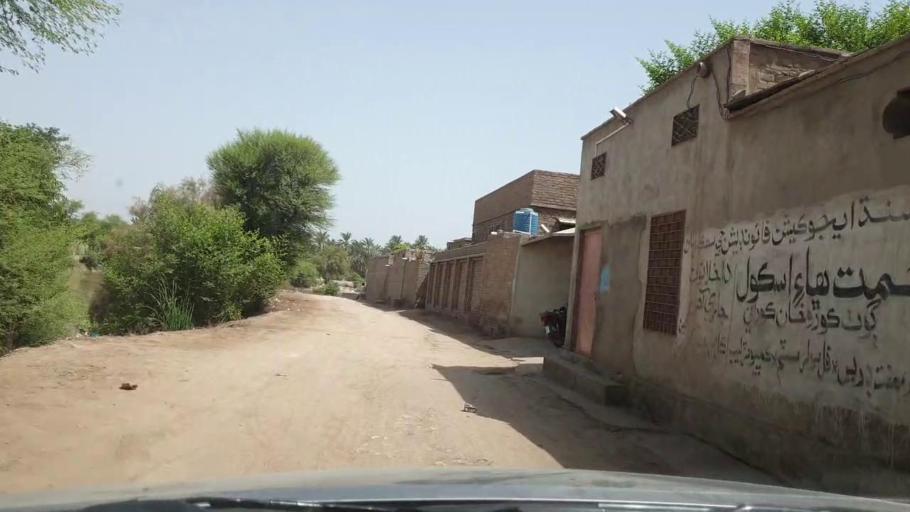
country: PK
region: Sindh
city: Pano Aqil
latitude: 27.9072
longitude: 69.1507
